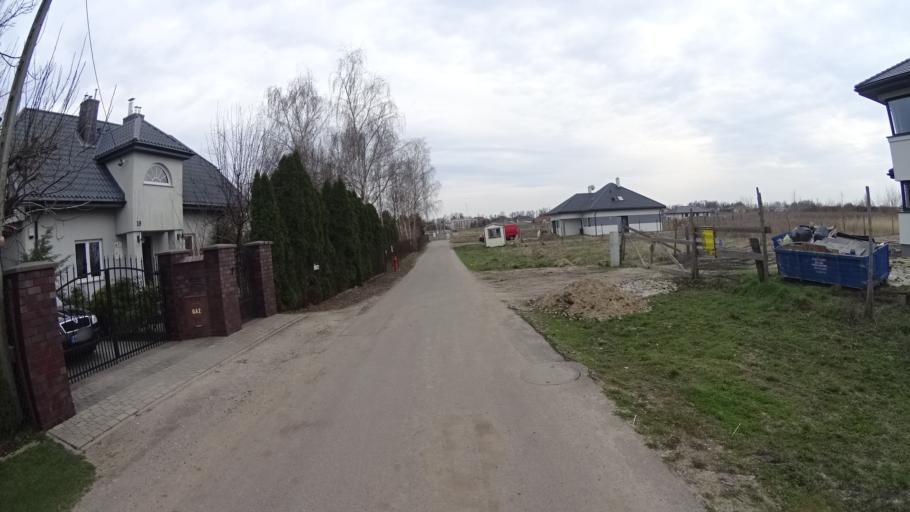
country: PL
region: Masovian Voivodeship
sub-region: Powiat warszawski zachodni
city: Jozefow
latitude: 52.2019
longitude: 20.6932
